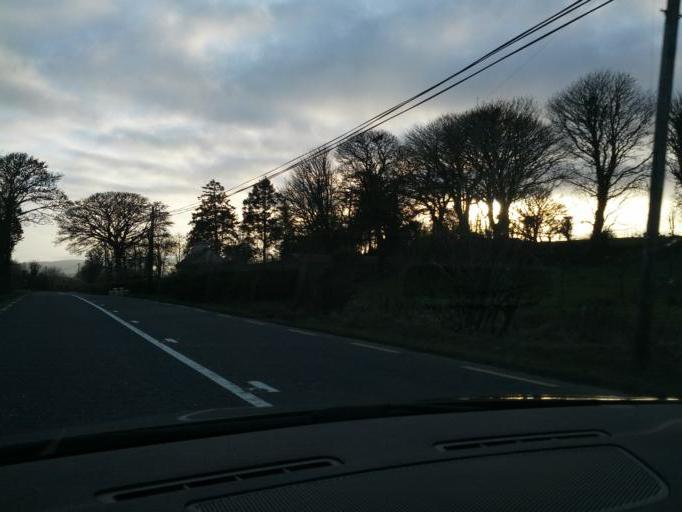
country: IE
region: Connaught
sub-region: Sligo
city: Ballymote
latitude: 54.1159
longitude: -8.6090
